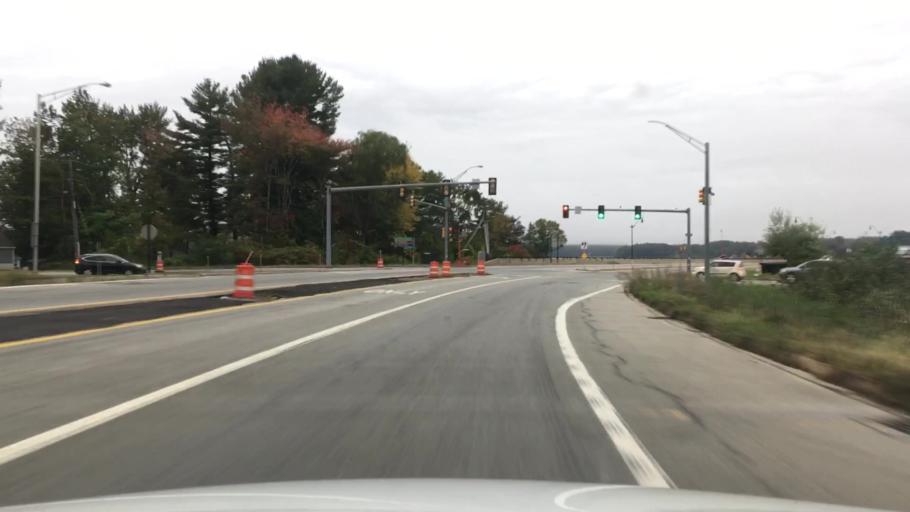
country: US
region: Maine
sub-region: York County
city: Eliot
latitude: 43.1285
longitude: -70.8429
